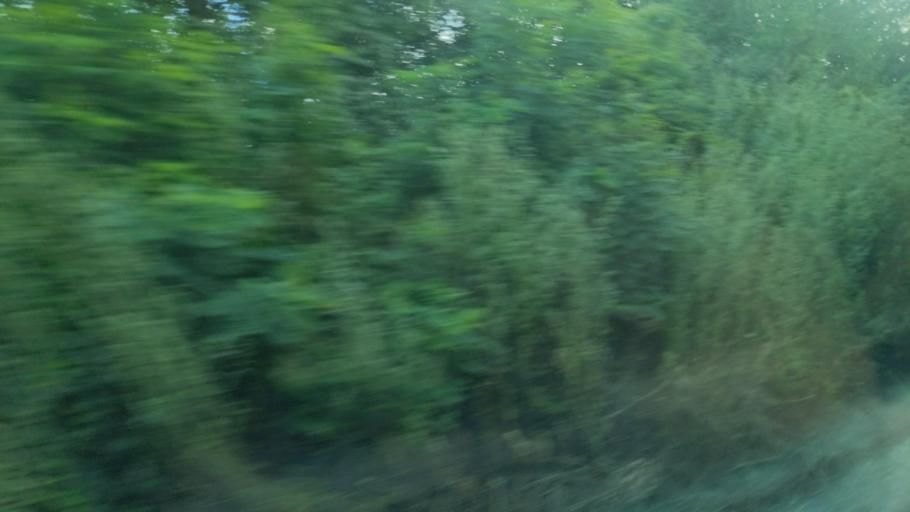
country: CZ
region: Central Bohemia
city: Uvaly
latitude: 50.0778
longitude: 14.7870
